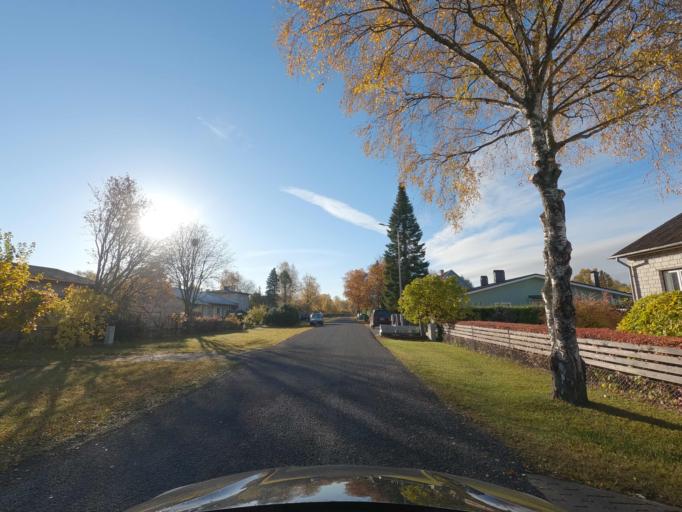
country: EE
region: Raplamaa
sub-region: Kohila vald
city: Kohila
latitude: 59.1640
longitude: 24.7675
